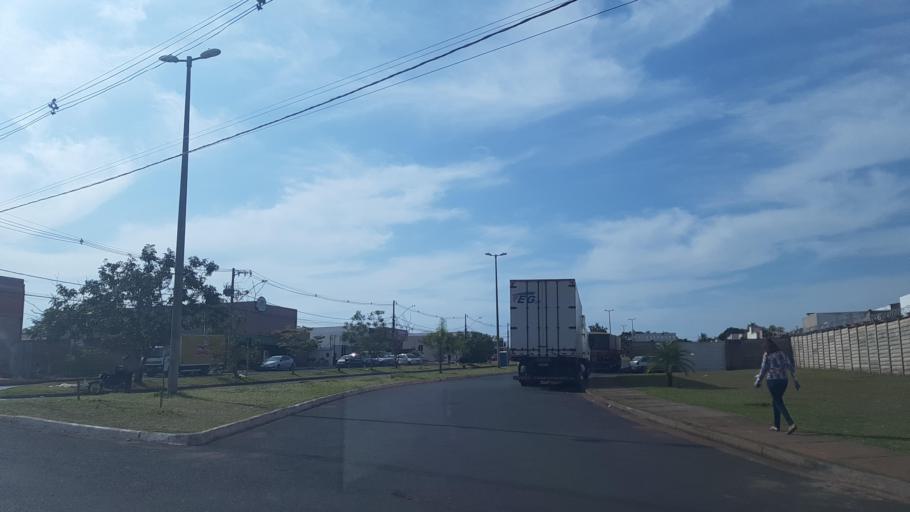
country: BR
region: Minas Gerais
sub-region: Uberlandia
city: Uberlandia
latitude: -18.8734
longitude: -48.2302
